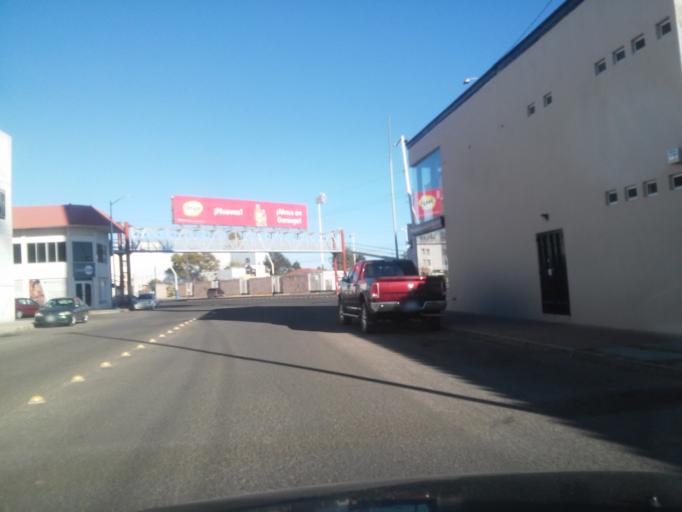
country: MX
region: Durango
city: Victoria de Durango
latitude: 24.0283
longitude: -104.6450
